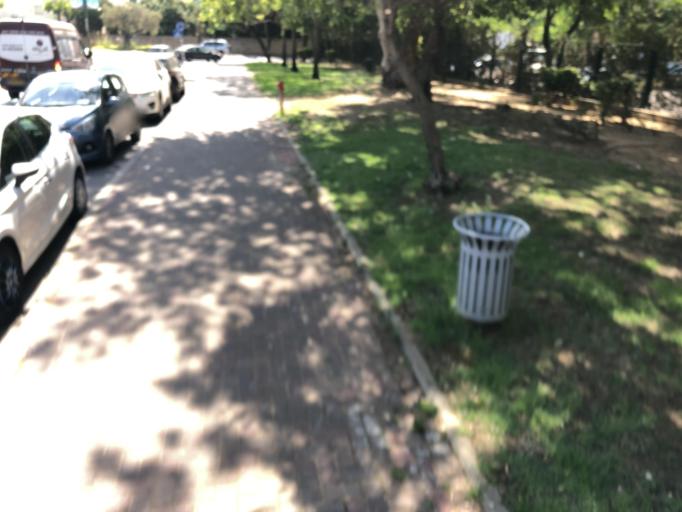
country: IL
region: Central District
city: Yehud
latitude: 32.0326
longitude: 34.8801
